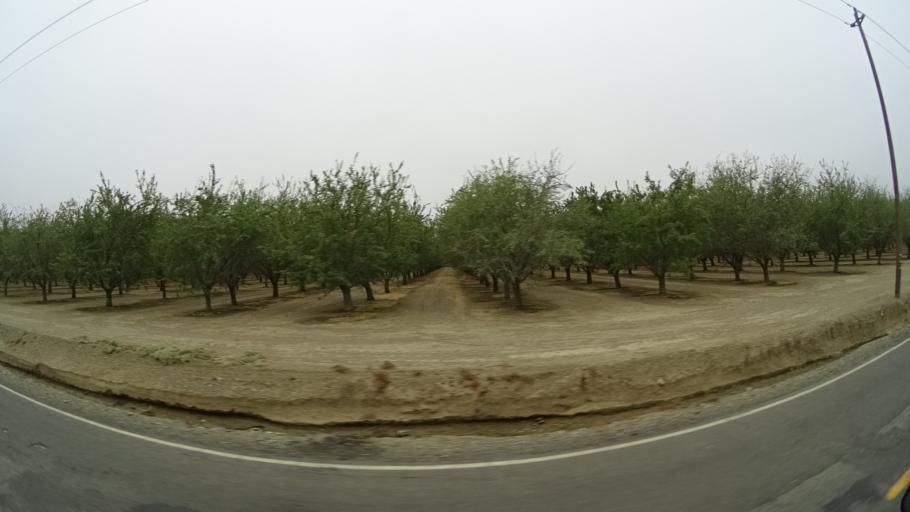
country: US
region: California
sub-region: Yolo County
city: Dunnigan
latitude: 38.9259
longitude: -122.0394
